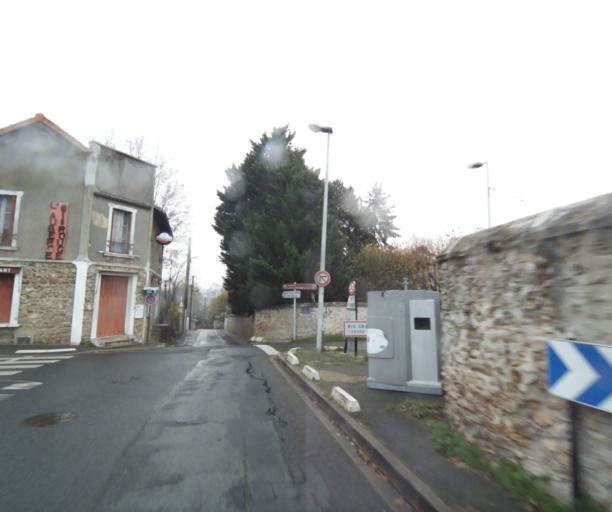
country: FR
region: Ile-de-France
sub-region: Departement de l'Essonne
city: Soisy-sur-Seine
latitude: 48.6454
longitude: 2.4335
